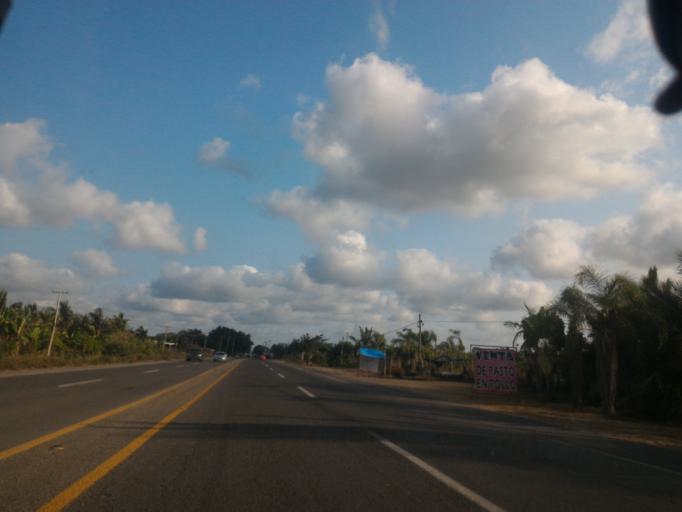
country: MX
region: Colima
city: Tecoman
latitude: 18.8710
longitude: -103.8420
